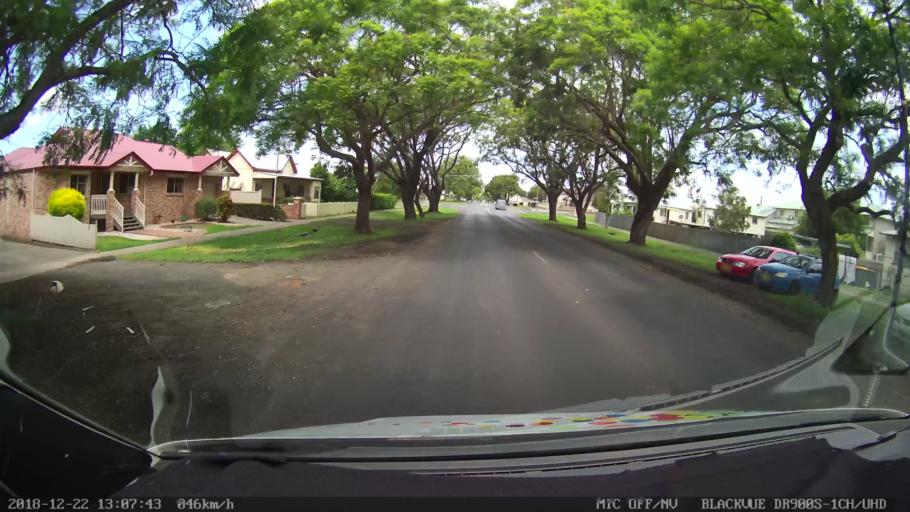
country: AU
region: New South Wales
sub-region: Clarence Valley
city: Grafton
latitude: -29.6861
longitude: 152.9294
